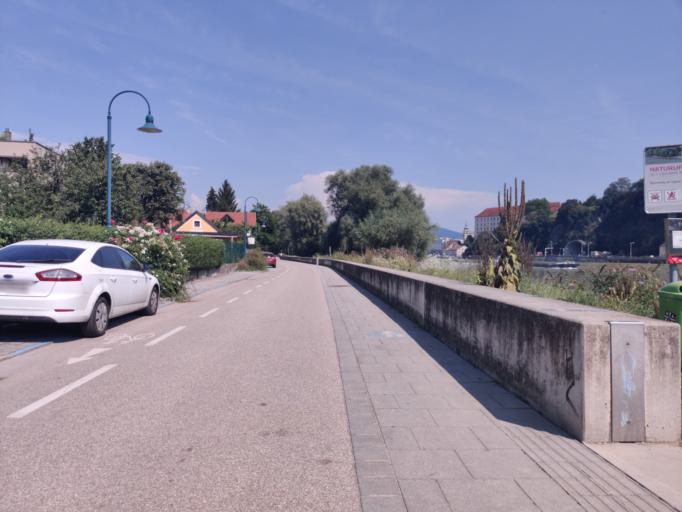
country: AT
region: Upper Austria
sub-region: Linz Stadt
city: Linz
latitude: 48.3062
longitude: 14.2742
